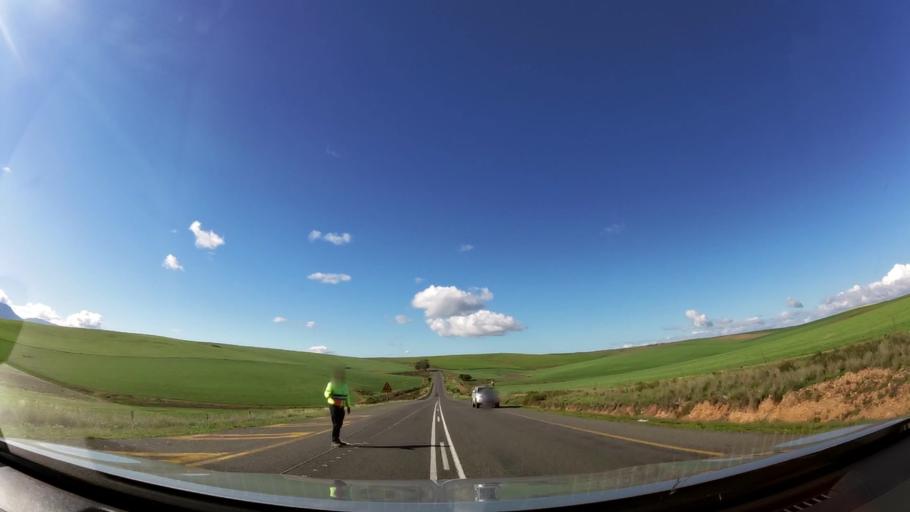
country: ZA
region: Western Cape
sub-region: Overberg District Municipality
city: Caledon
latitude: -34.1829
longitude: 19.6927
